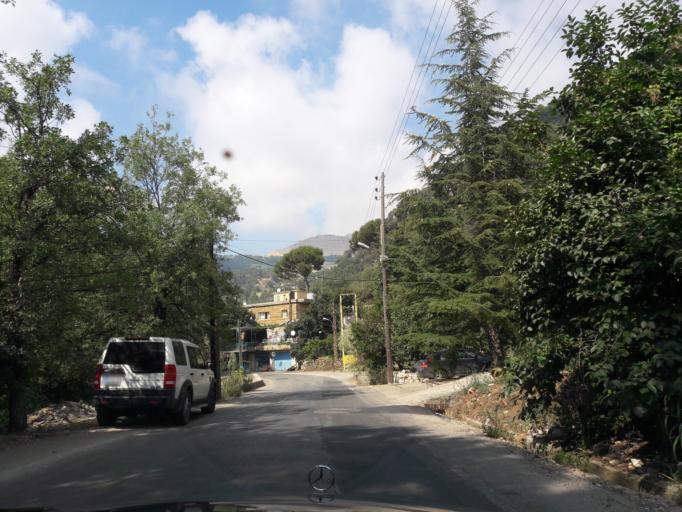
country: LB
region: Mont-Liban
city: Djounie
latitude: 33.9610
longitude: 35.7796
